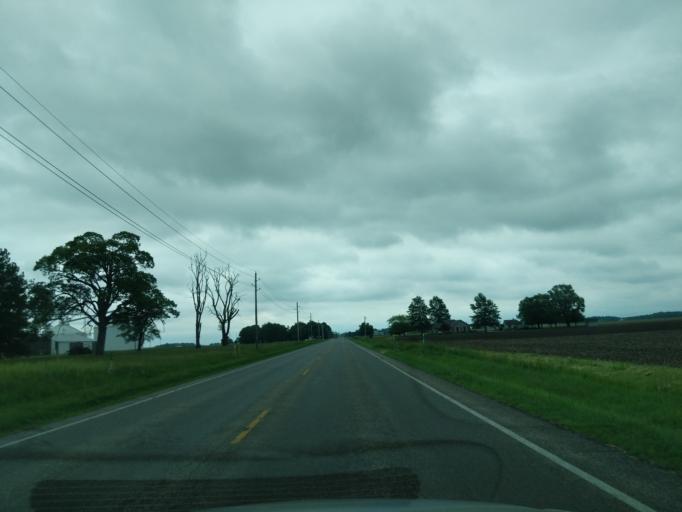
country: US
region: Indiana
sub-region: Tipton County
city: Tipton
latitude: 40.2834
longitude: -86.0088
